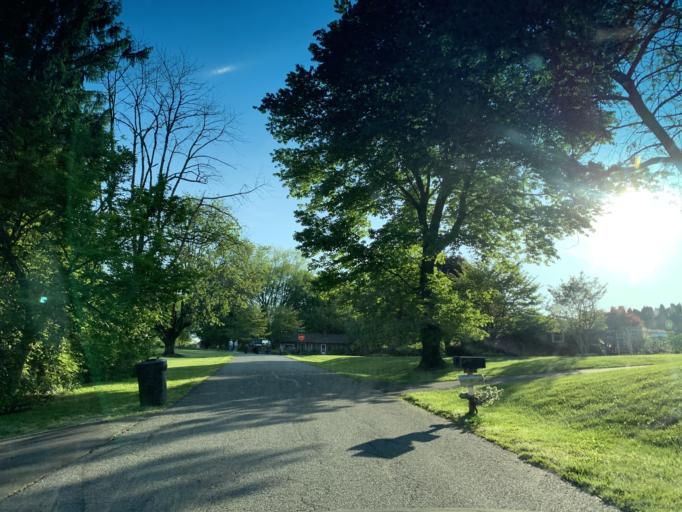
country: US
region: Maryland
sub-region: Harford County
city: Bel Air South
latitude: 39.5116
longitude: -76.2934
